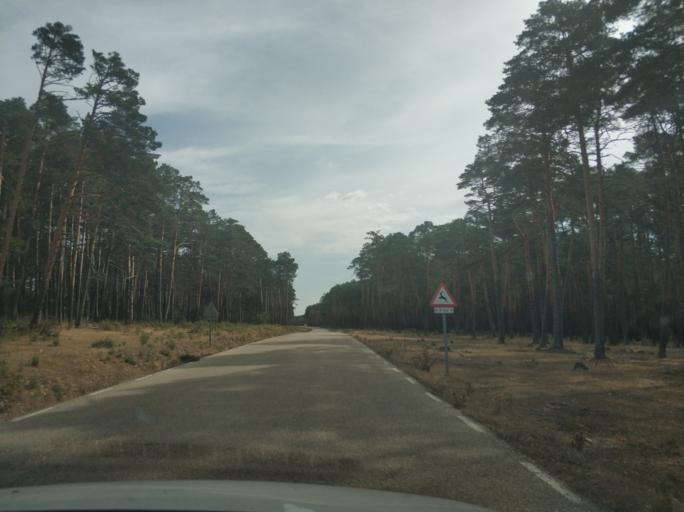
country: ES
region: Castille and Leon
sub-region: Provincia de Soria
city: Navaleno
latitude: 41.8536
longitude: -2.9593
